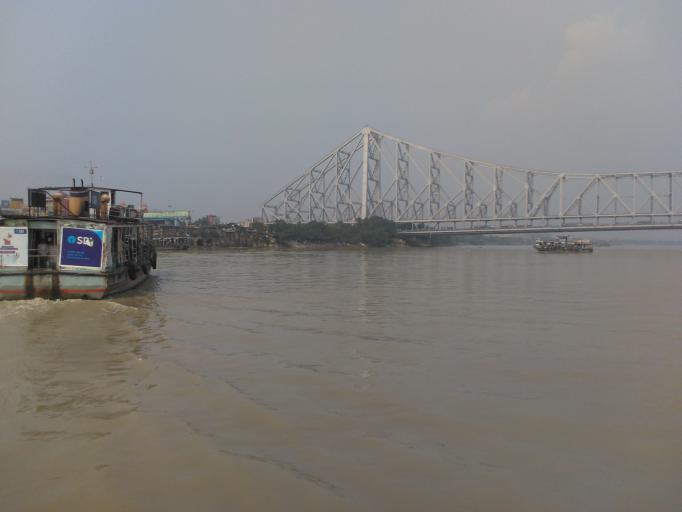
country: IN
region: West Bengal
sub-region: Kolkata
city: Bara Bazar
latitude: 22.5817
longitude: 88.3454
